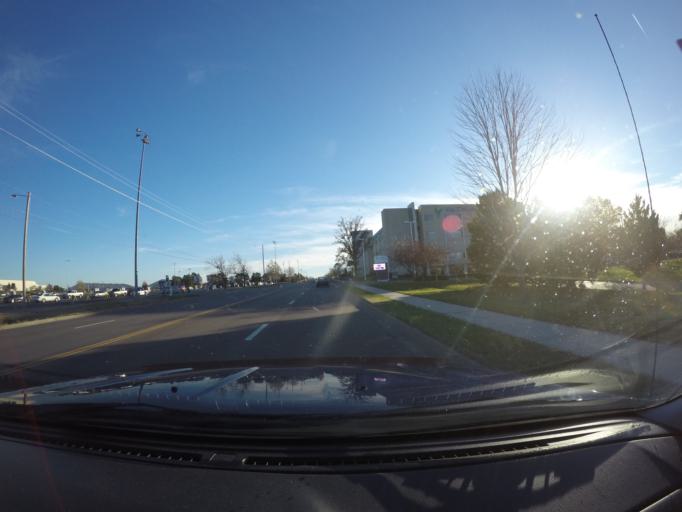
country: US
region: Kansas
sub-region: Riley County
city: Manhattan
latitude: 39.2025
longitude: -96.5983
